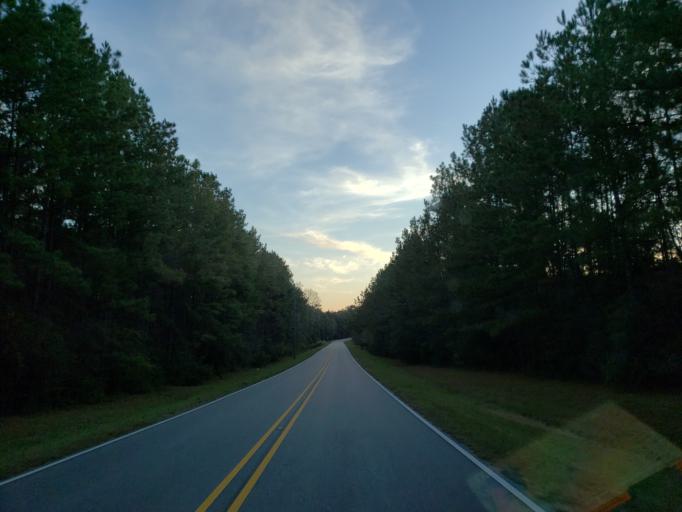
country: US
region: Mississippi
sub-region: Forrest County
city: Hattiesburg
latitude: 31.2674
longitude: -89.3097
